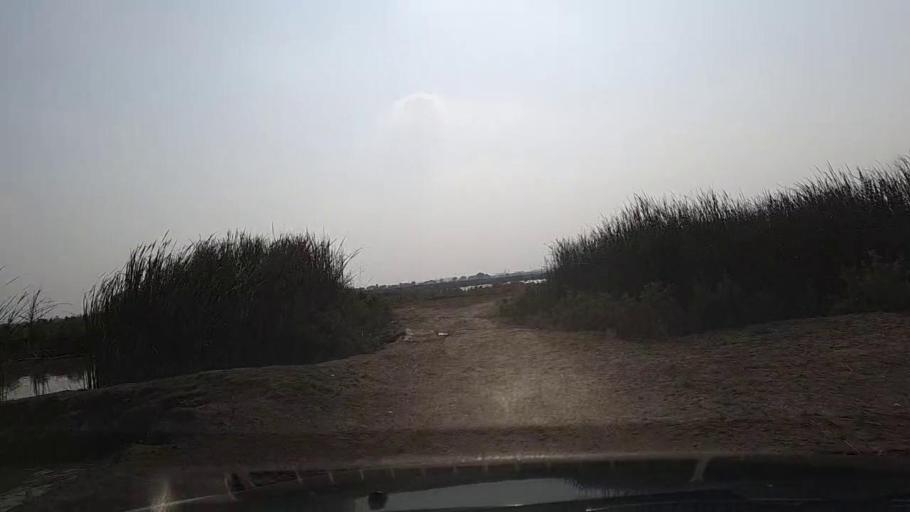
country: PK
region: Sindh
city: Mirpur Batoro
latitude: 24.6457
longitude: 68.2819
